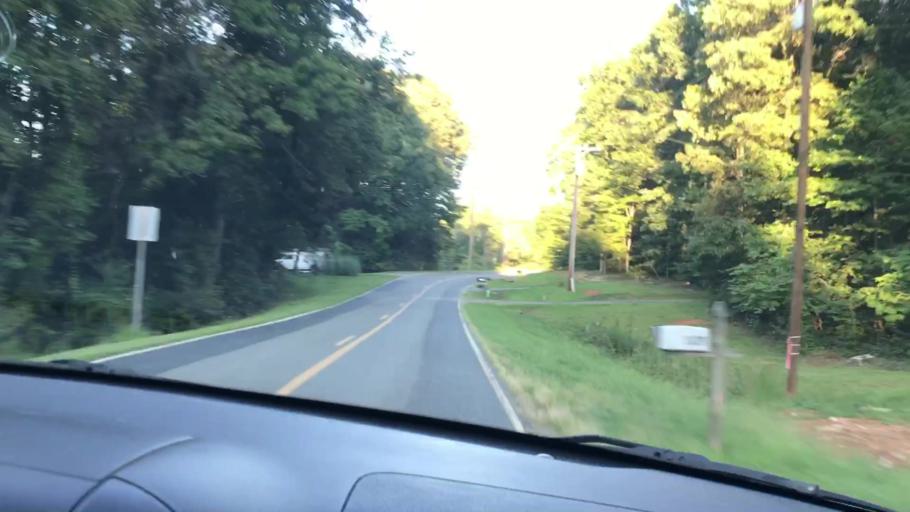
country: US
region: North Carolina
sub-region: Randolph County
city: Franklinville
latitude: 35.8109
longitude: -79.6939
